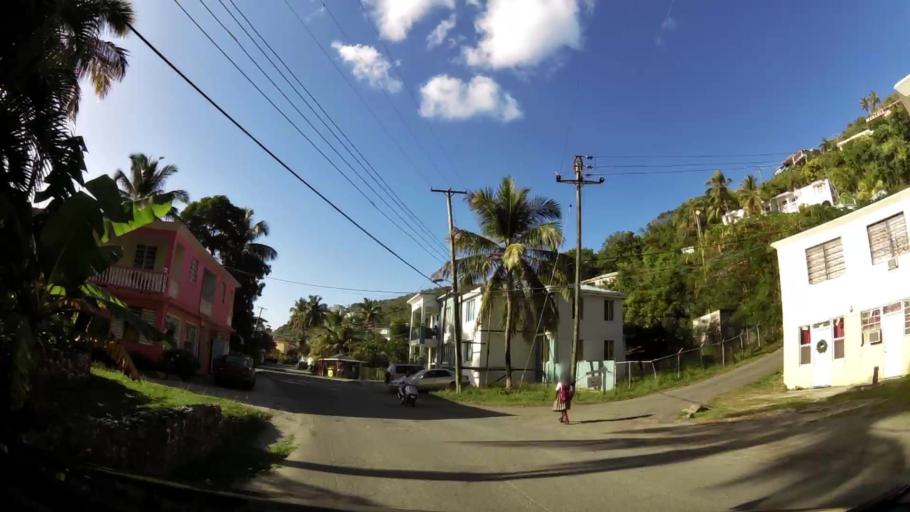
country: VG
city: Road Town
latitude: 18.4268
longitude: -64.6561
